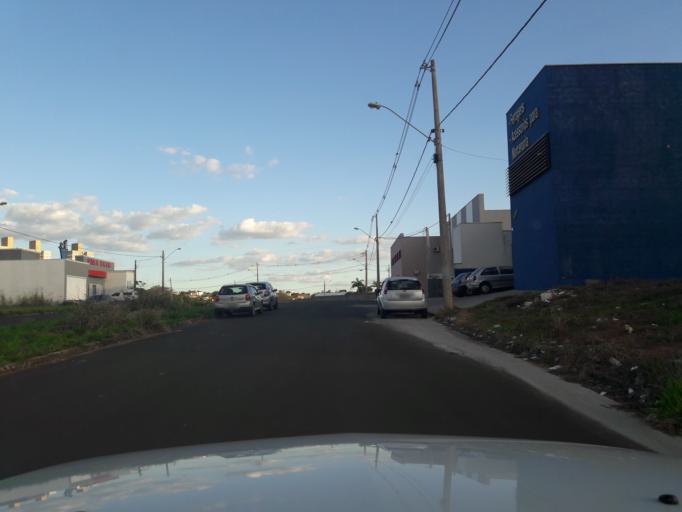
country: BR
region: Sao Paulo
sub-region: Moji-Guacu
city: Mogi-Gaucu
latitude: -22.3925
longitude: -46.9521
